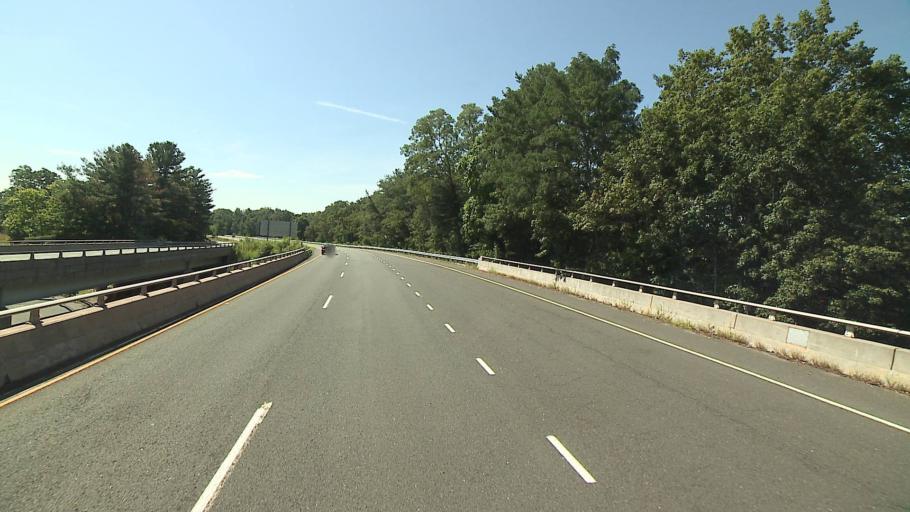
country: US
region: Connecticut
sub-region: Hartford County
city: Tariffville
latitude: 41.8881
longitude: -72.7488
